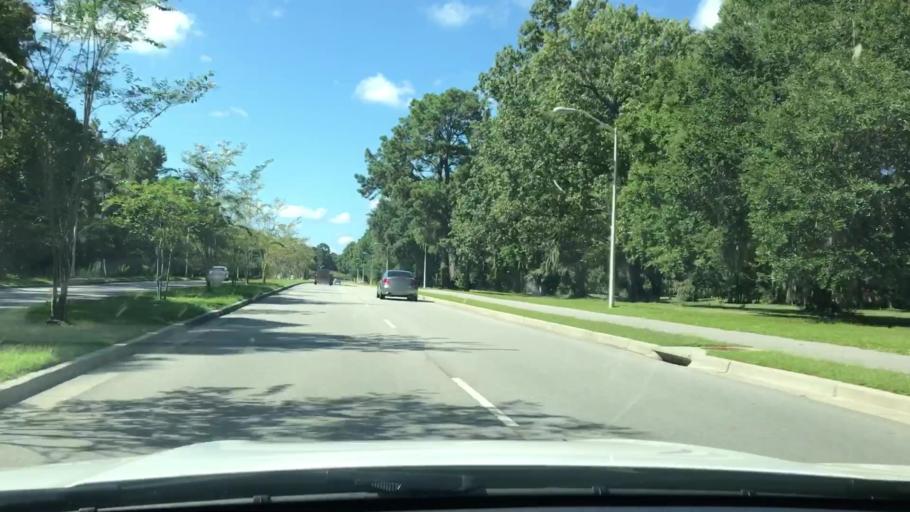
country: US
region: South Carolina
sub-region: Charleston County
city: Shell Point
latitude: 32.8388
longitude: -80.0647
